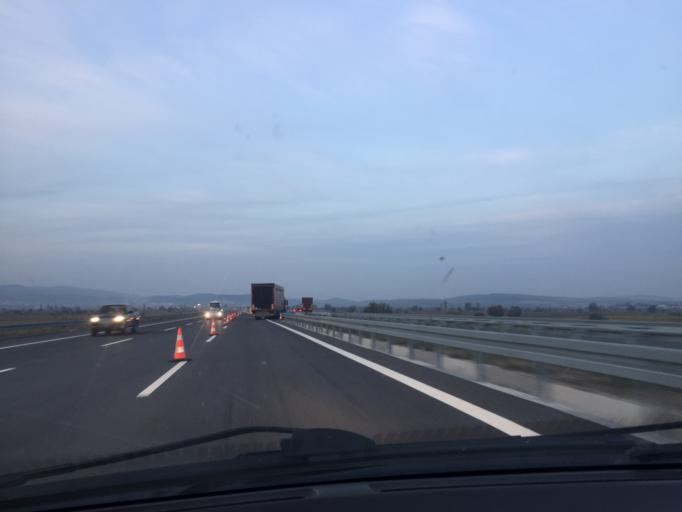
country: TR
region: Manisa
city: Halitpasa
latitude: 38.7427
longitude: 27.6586
